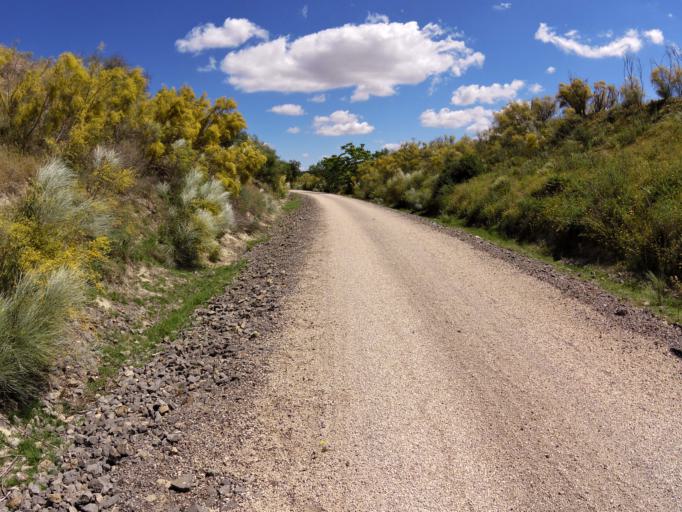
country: ES
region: Andalusia
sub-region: Provincia de Jaen
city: Alcaudete
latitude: 37.6502
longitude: -4.0627
